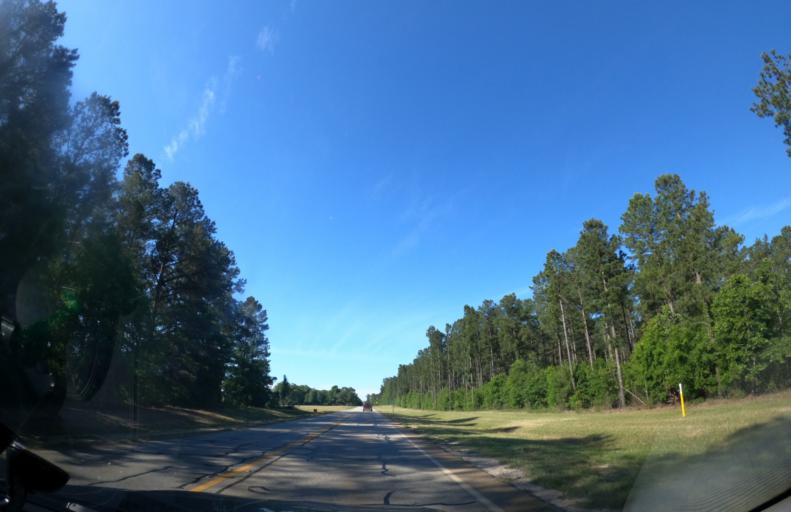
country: US
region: Georgia
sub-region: Jefferson County
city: Wrens
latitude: 33.2599
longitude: -82.3852
